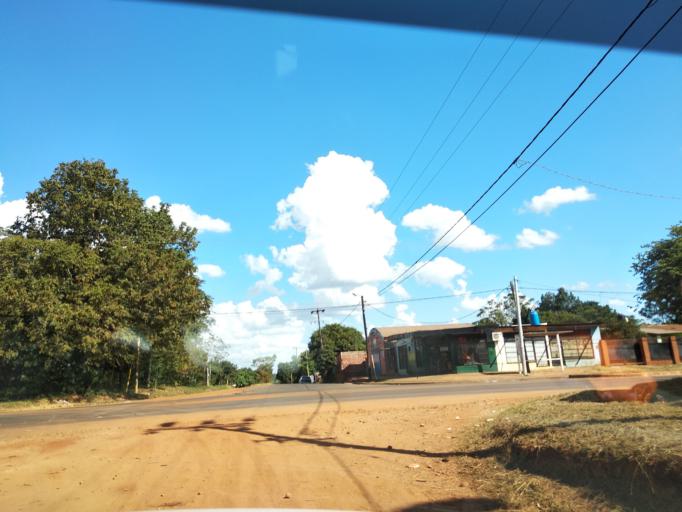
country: AR
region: Misiones
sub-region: Departamento de Capital
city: Posadas
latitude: -27.3825
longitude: -55.9453
